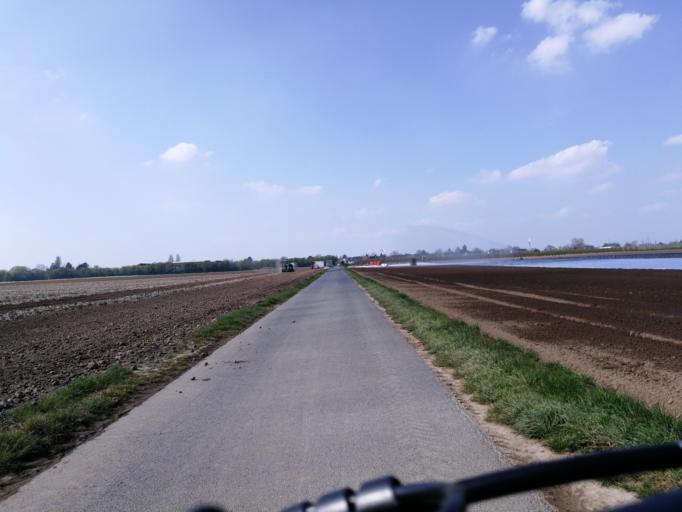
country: DE
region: North Rhine-Westphalia
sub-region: Regierungsbezirk Dusseldorf
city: Dormagen
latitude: 51.1156
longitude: 6.7875
